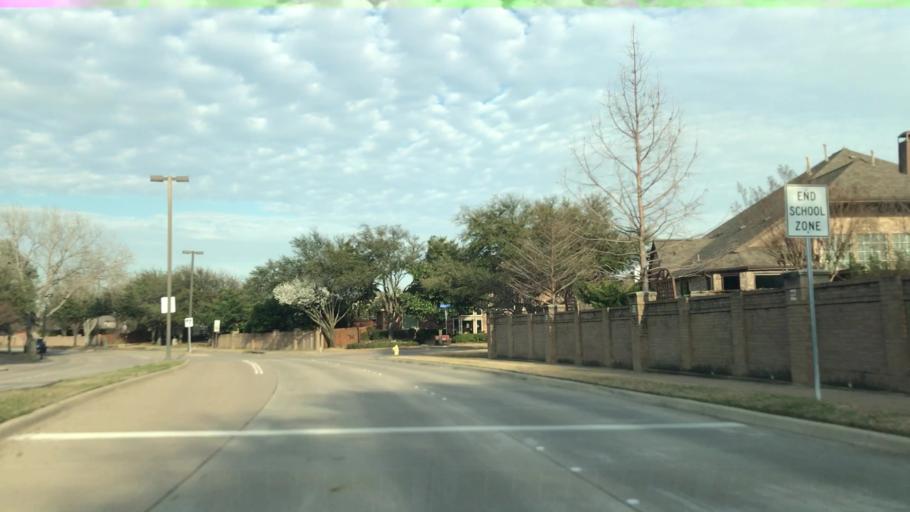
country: US
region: Texas
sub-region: Dallas County
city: Coppell
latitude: 32.9793
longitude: -97.0063
